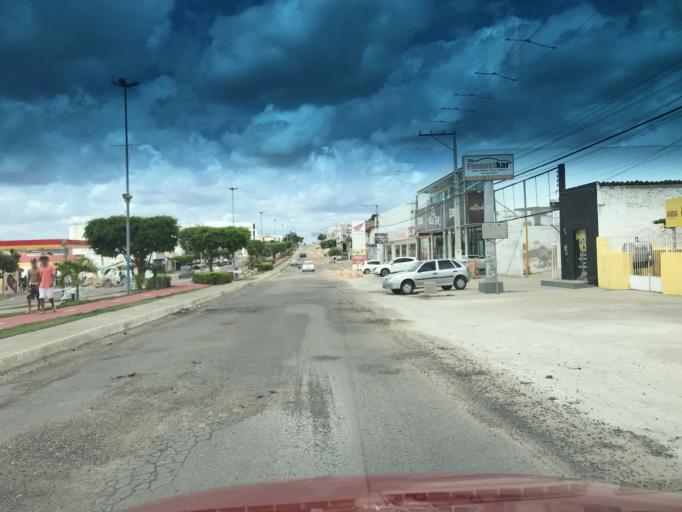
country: BR
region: Bahia
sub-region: Itaberaba
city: Itaberaba
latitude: -12.5223
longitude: -40.3062
